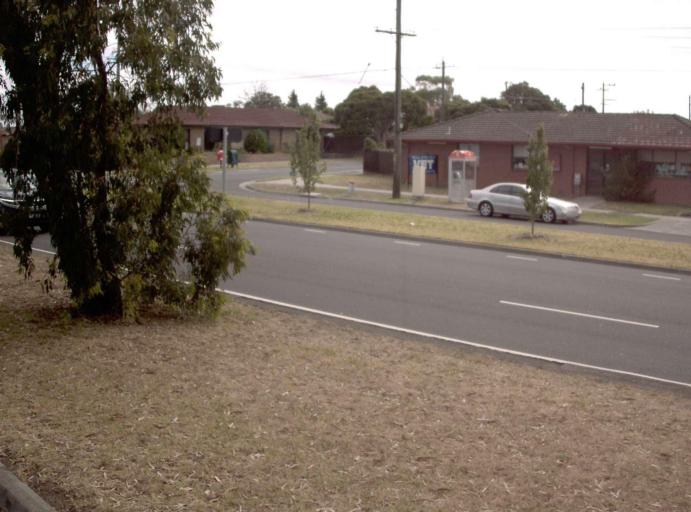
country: AU
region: Victoria
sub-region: Greater Dandenong
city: Dandenong North
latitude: -37.9648
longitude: 145.2246
